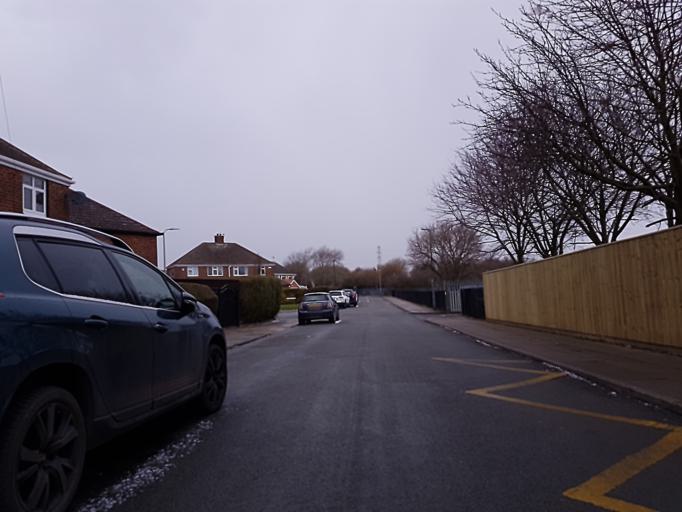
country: GB
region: England
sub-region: North East Lincolnshire
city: Grimbsy
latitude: 53.5632
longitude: -0.1164
